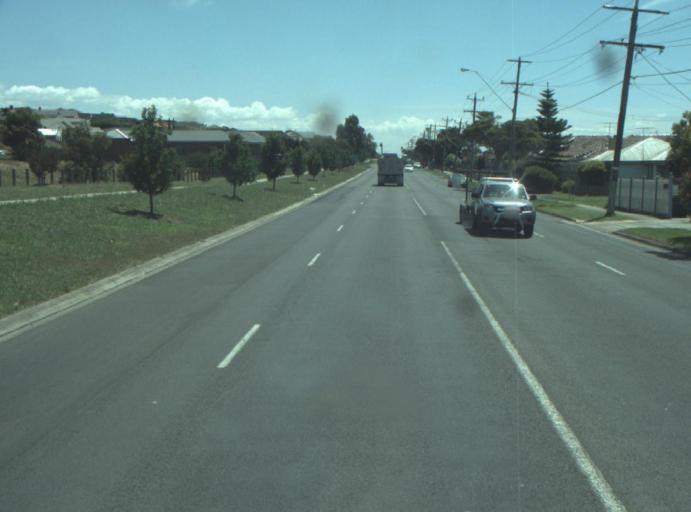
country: AU
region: Victoria
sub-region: Greater Geelong
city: Bell Park
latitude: -38.1127
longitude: 144.3312
